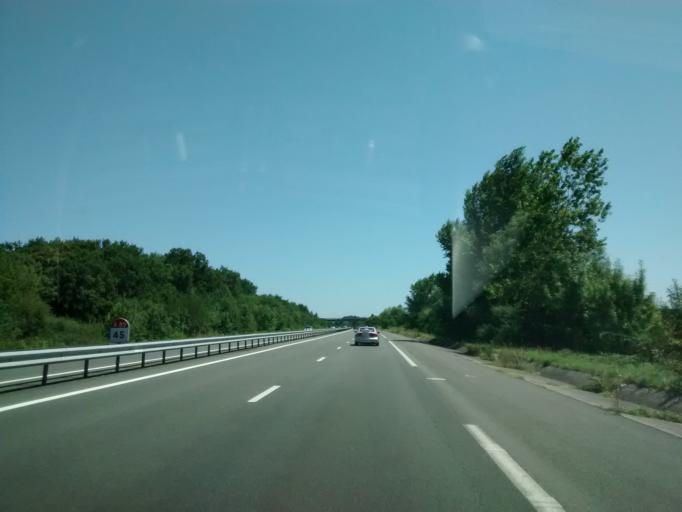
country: FR
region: Aquitaine
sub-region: Departement de la Gironde
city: Saint-Medard-de-Guizieres
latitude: 45.0071
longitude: -0.0765
